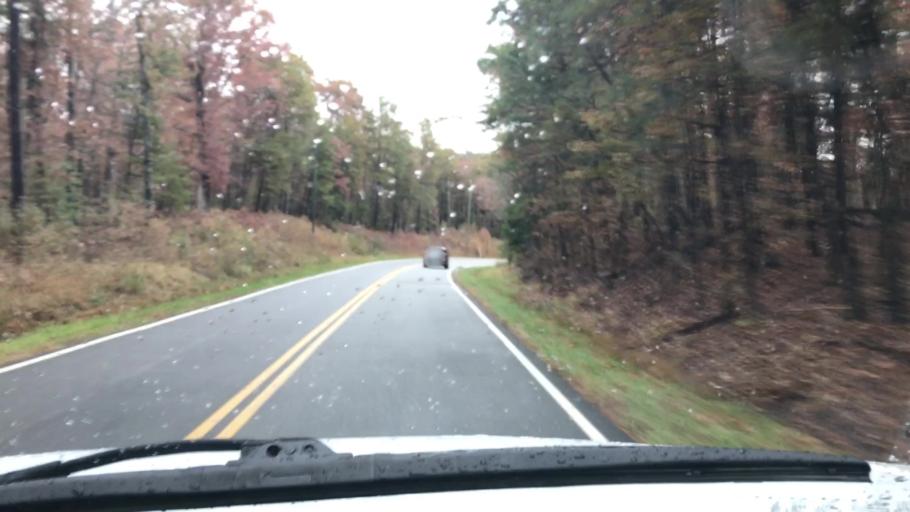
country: US
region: Virginia
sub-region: Henrico County
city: Short Pump
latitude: 37.6087
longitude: -77.6990
